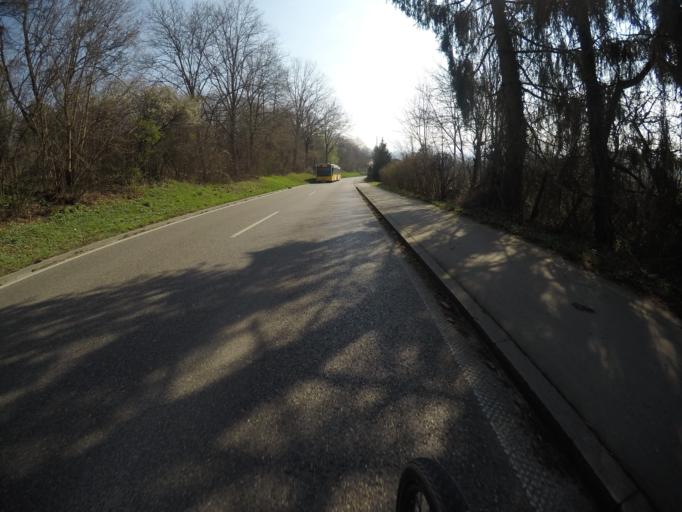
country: DE
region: Baden-Wuerttemberg
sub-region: Regierungsbezirk Stuttgart
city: Nurtingen
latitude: 48.6416
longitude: 9.3143
